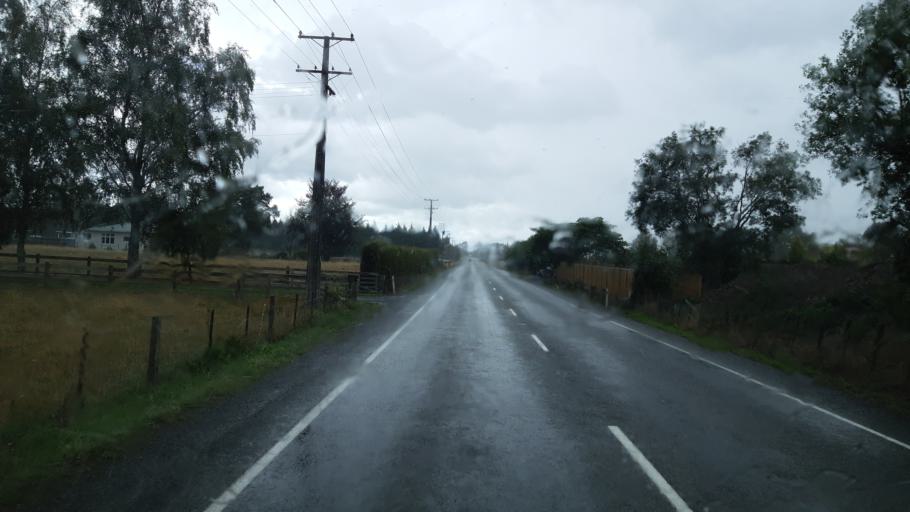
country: NZ
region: Tasman
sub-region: Tasman District
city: Wakefield
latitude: -41.3888
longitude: 173.0750
